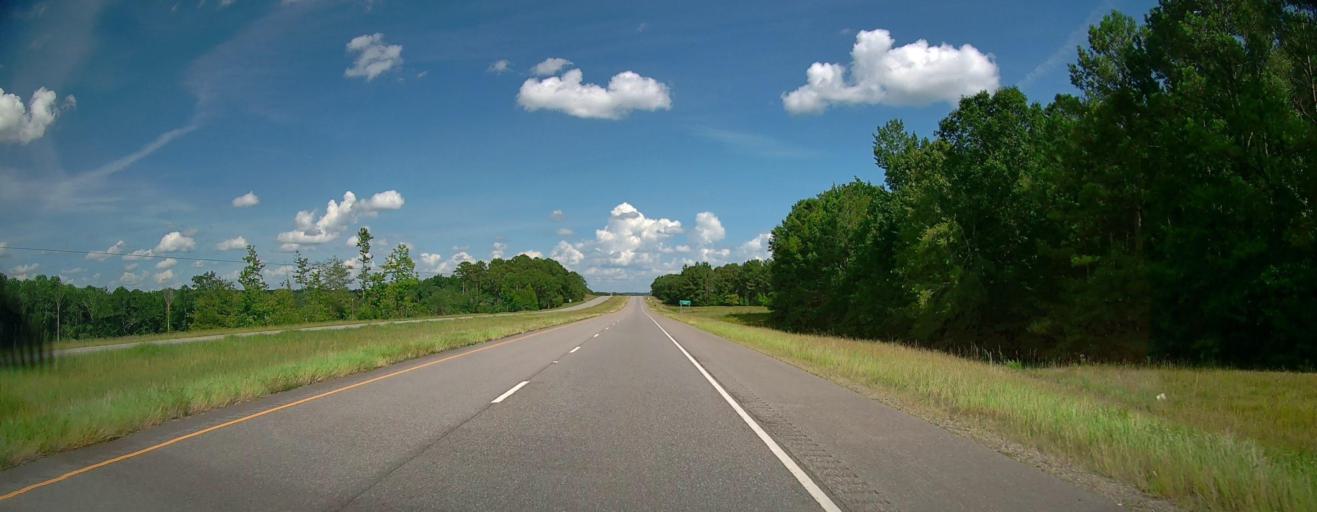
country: US
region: Alabama
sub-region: Pickens County
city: Reform
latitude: 33.3942
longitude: -88.0517
